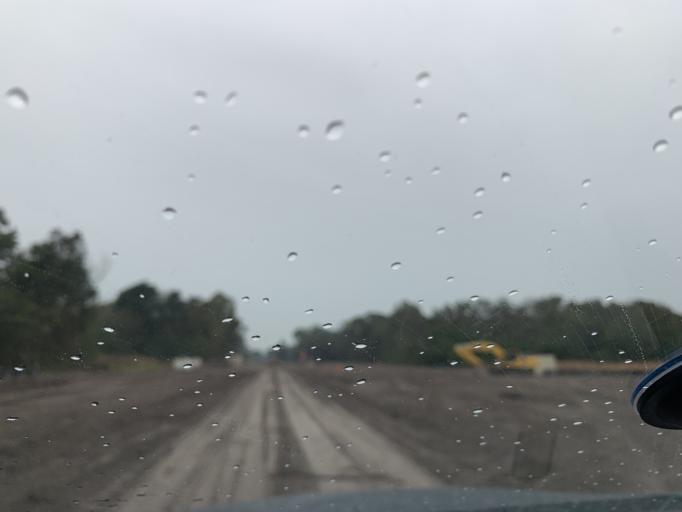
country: US
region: Florida
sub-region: Hernando County
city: Masaryktown
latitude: 28.4518
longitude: -82.4565
